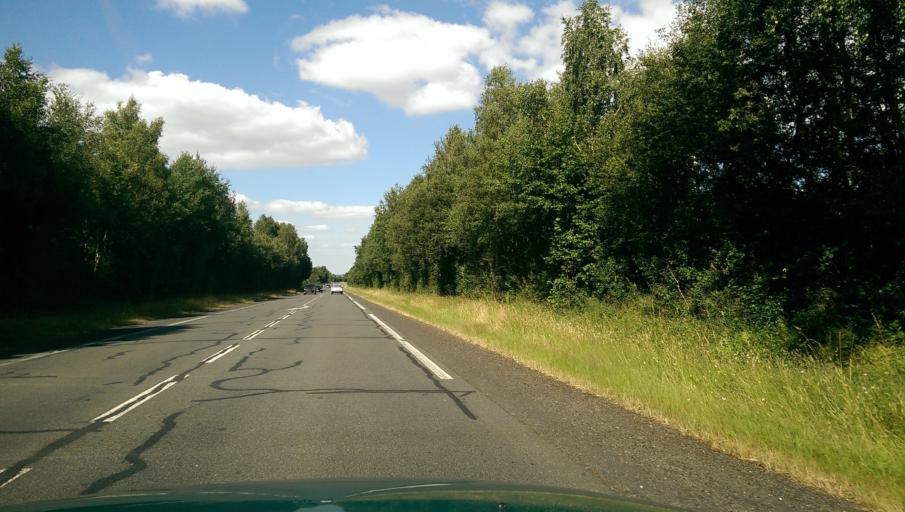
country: FR
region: Pays de la Loire
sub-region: Departement de la Loire-Atlantique
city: Lege
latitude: 46.8855
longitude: -1.6142
